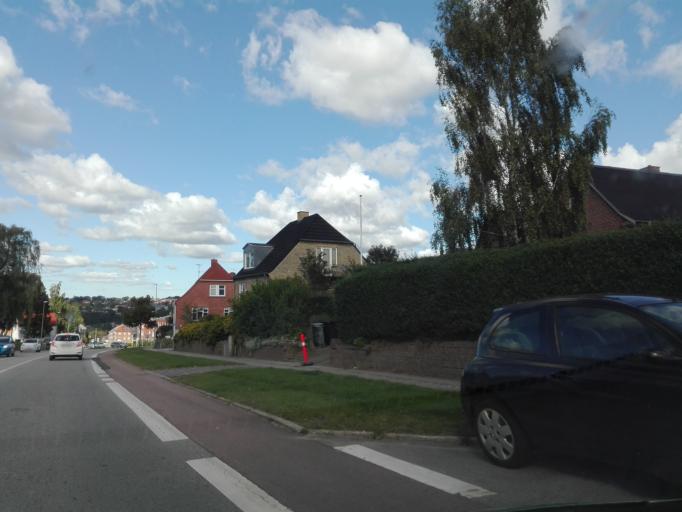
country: DK
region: North Denmark
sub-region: Mariagerfjord Kommune
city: Hobro
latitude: 56.6322
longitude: 9.8005
